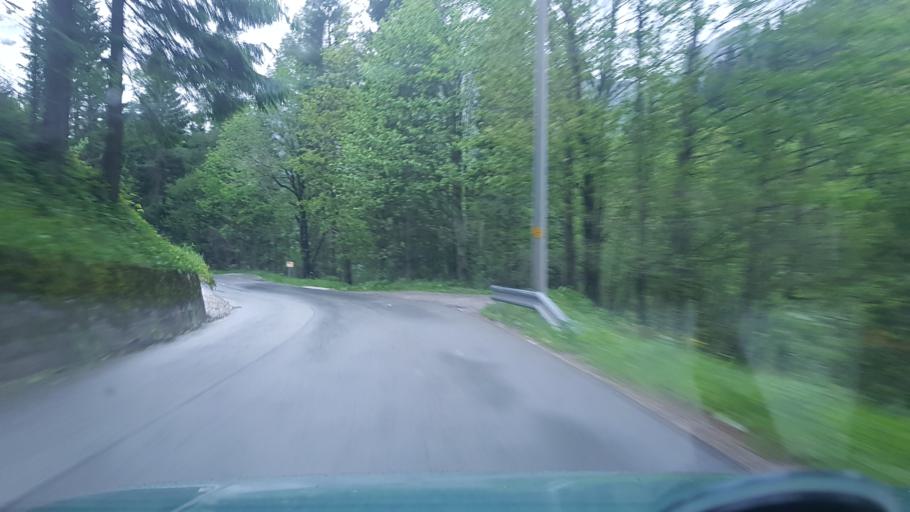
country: SI
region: Bohinj
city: Bohinjska Bistrica
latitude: 46.2127
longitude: 13.9934
